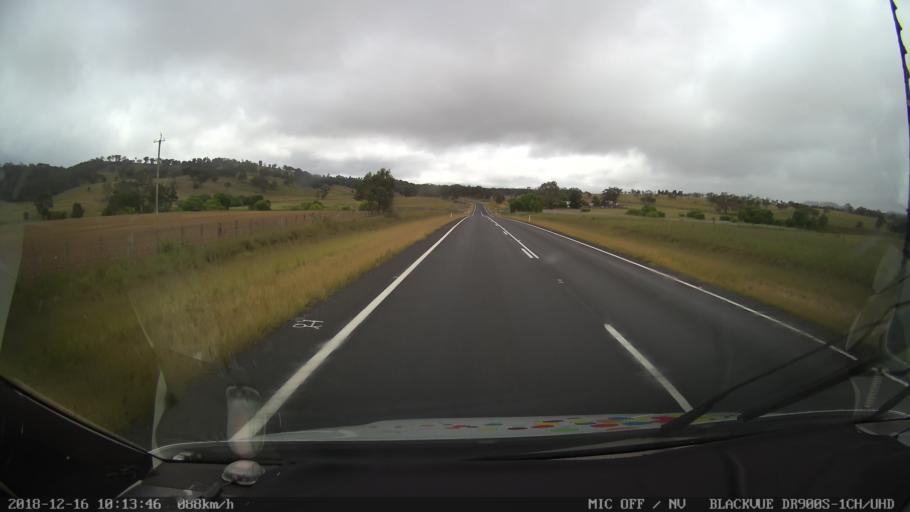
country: AU
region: New South Wales
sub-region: Glen Innes Severn
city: Glen Innes
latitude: -29.2940
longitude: 151.9565
